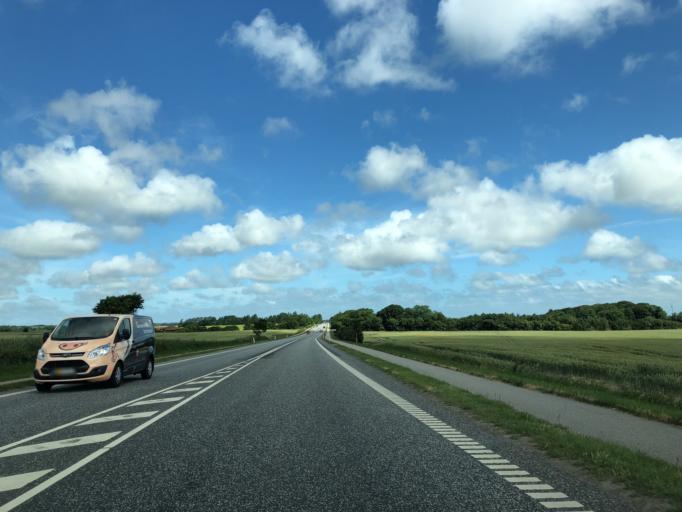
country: DK
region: Central Jutland
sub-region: Struer Kommune
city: Struer
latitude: 56.4305
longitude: 8.5980
